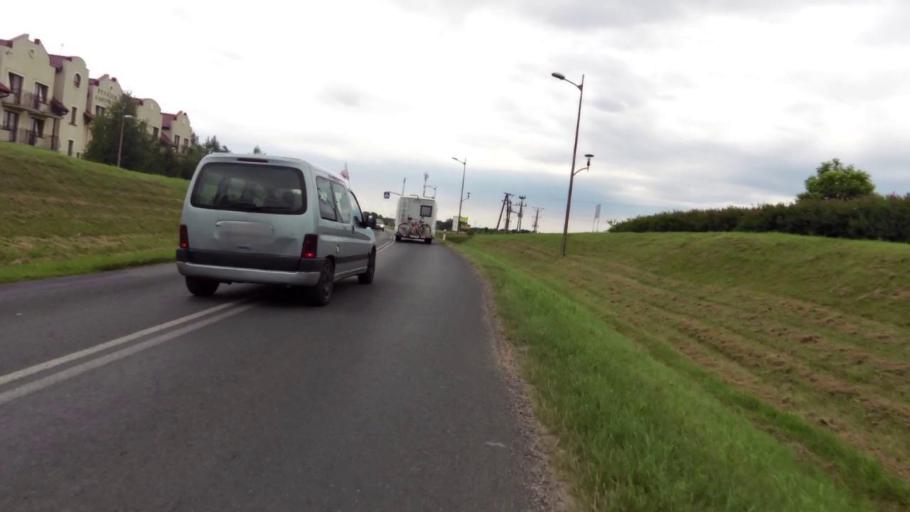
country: PL
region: West Pomeranian Voivodeship
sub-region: Powiat gryficki
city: Rewal
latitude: 54.0796
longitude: 15.0253
